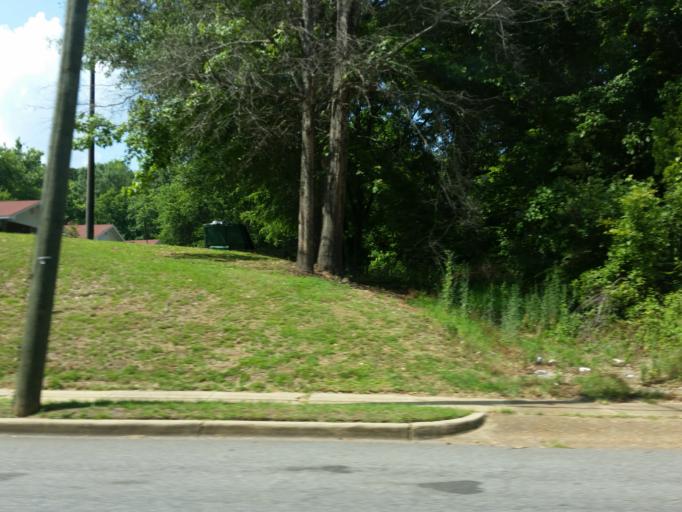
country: US
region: Alabama
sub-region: Greene County
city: Eutaw
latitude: 32.8404
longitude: -87.8824
